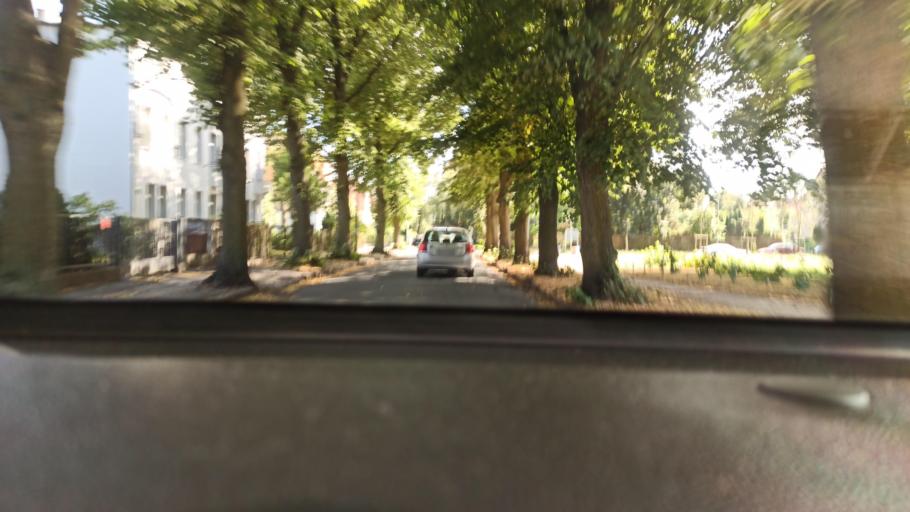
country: PL
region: West Pomeranian Voivodeship
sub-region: Szczecin
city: Szczecin
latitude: 53.4401
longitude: 14.5060
